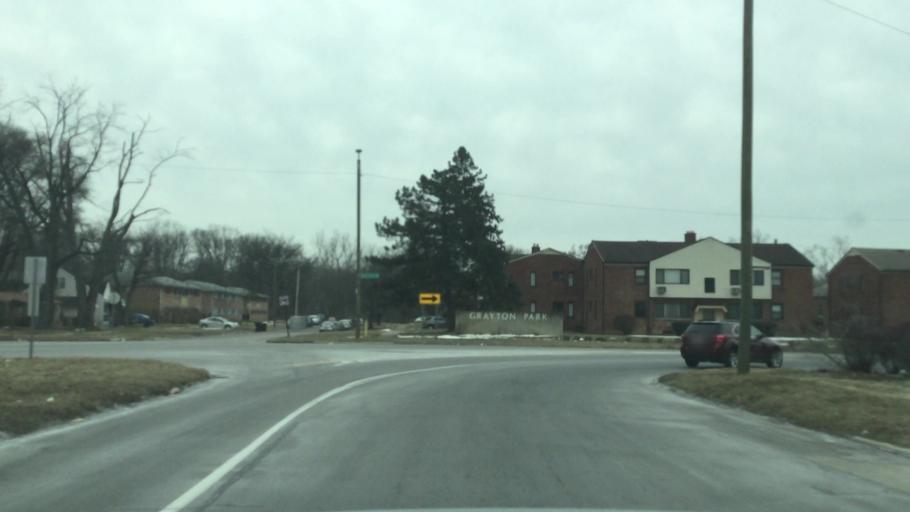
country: US
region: Michigan
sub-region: Wayne County
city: Redford
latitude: 42.3840
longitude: -83.2564
